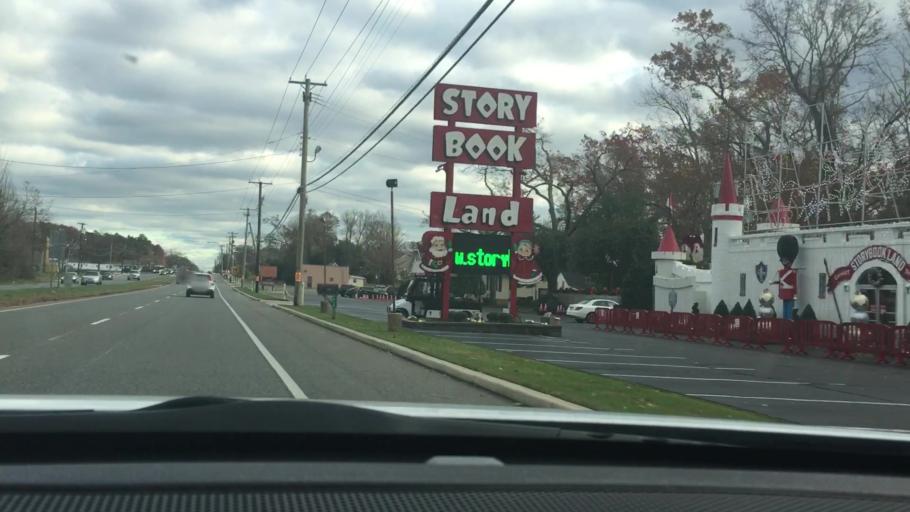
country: US
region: New Jersey
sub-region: Atlantic County
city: Pomona
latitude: 39.4235
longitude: -74.5914
